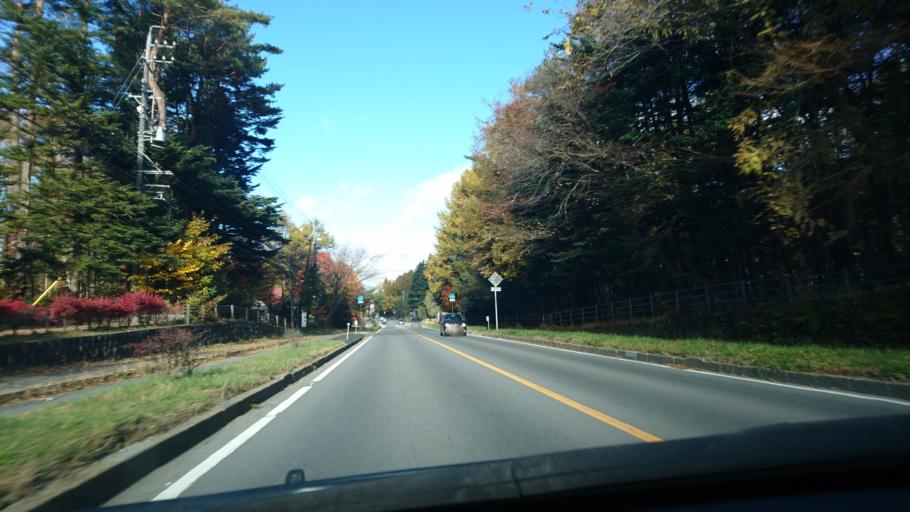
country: JP
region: Nagano
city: Saku
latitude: 36.3290
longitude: 138.6125
